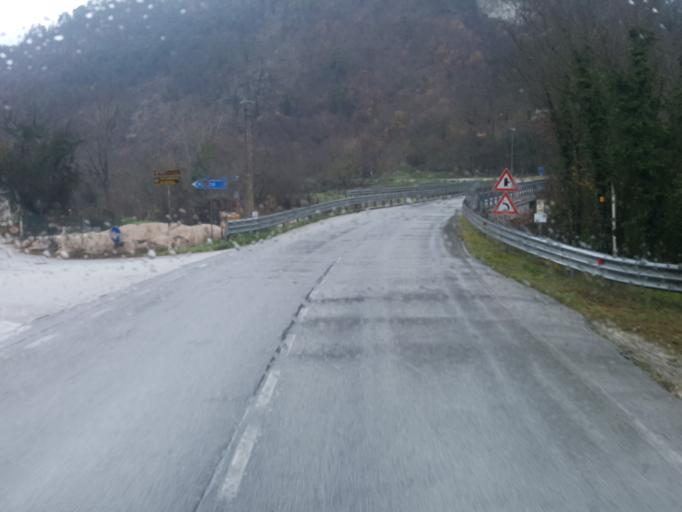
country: IT
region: The Marches
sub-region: Provincia di Ancona
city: Genga
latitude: 43.4259
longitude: 12.9326
